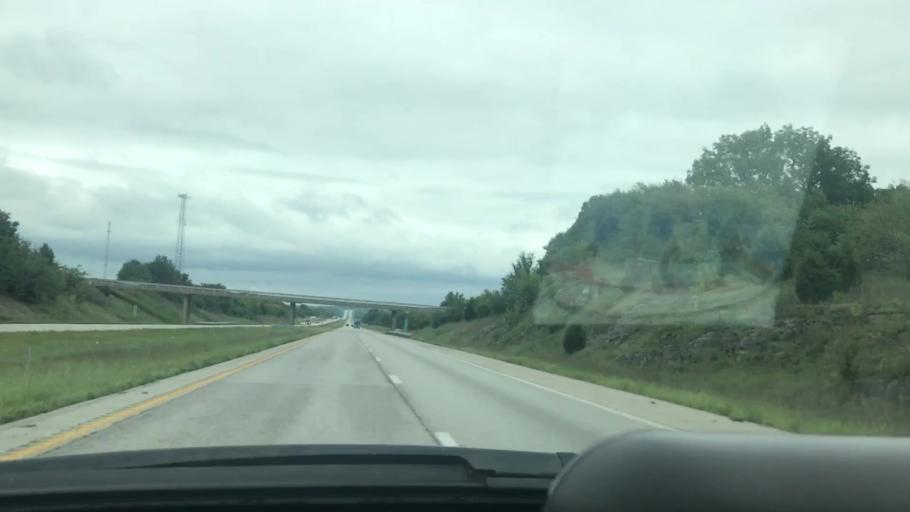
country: US
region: Missouri
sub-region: Lawrence County
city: Mount Vernon
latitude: 37.1539
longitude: -93.6978
